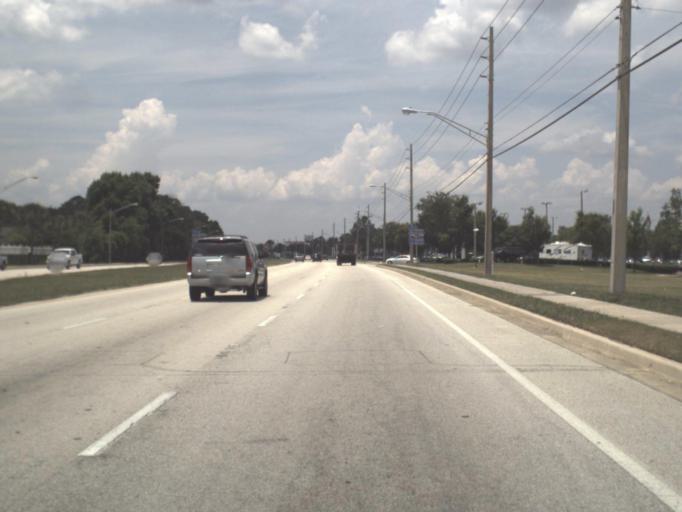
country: US
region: Florida
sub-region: Duval County
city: Atlantic Beach
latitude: 30.3243
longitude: -81.5078
